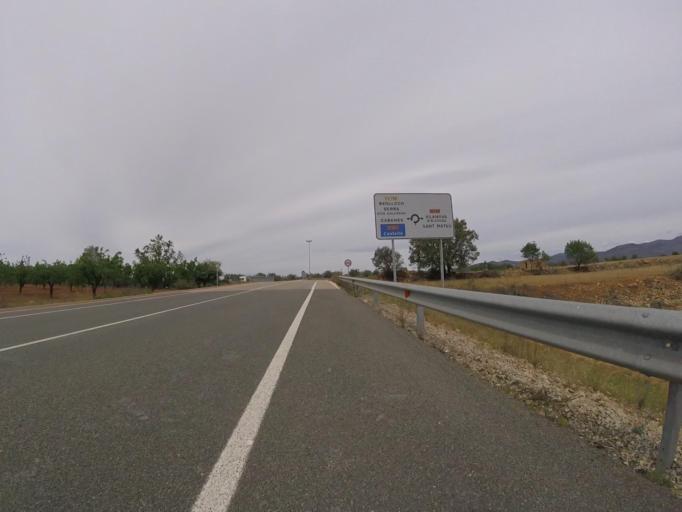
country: ES
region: Valencia
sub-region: Provincia de Castello
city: Benlloch
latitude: 40.1990
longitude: 0.0466
